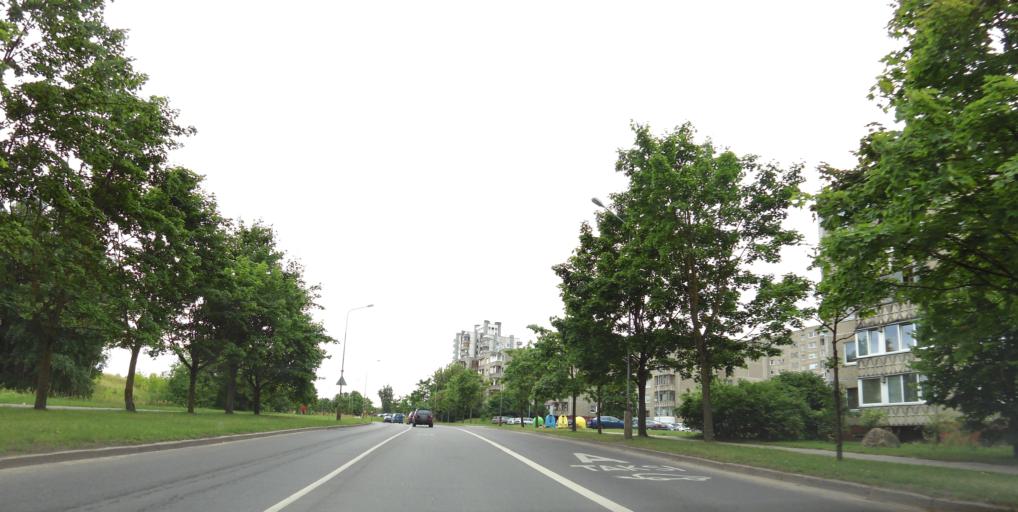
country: LT
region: Vilnius County
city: Seskine
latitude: 54.7139
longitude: 25.2566
